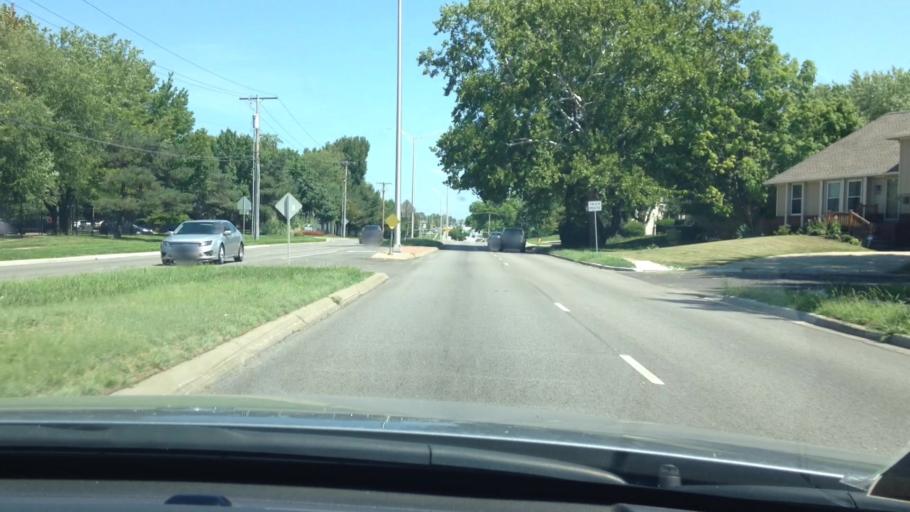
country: US
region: Kansas
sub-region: Johnson County
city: Overland Park
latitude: 38.9567
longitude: -94.6759
